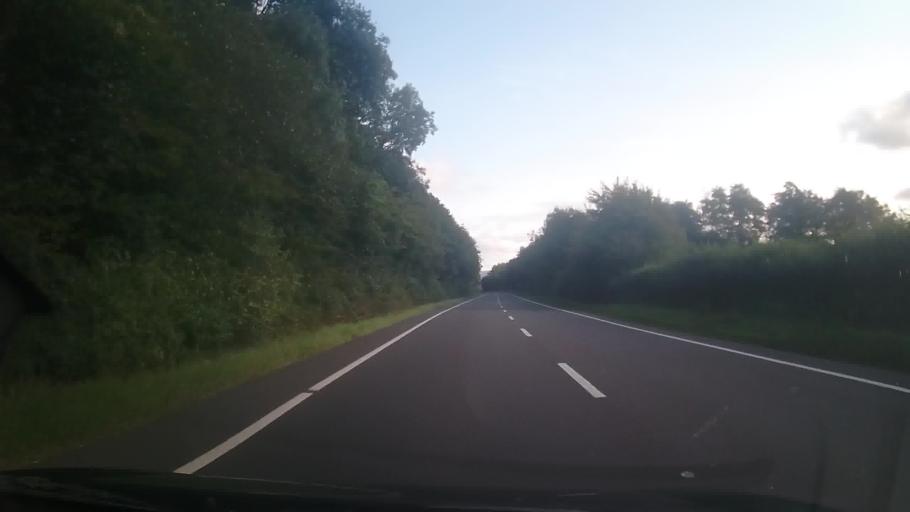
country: GB
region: England
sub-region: Shropshire
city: Craven Arms
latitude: 52.4125
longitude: -2.8094
